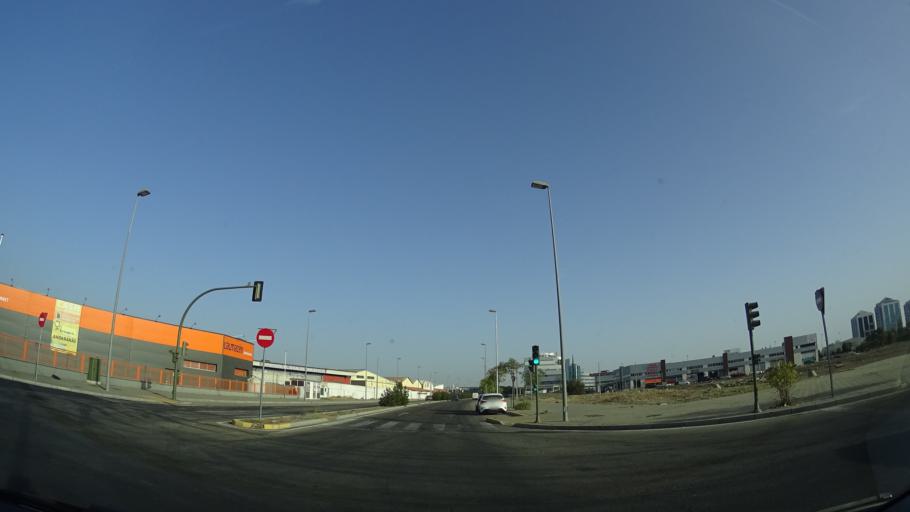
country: ES
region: Andalusia
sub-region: Provincia de Sevilla
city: Sevilla
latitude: 37.4240
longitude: -5.9781
